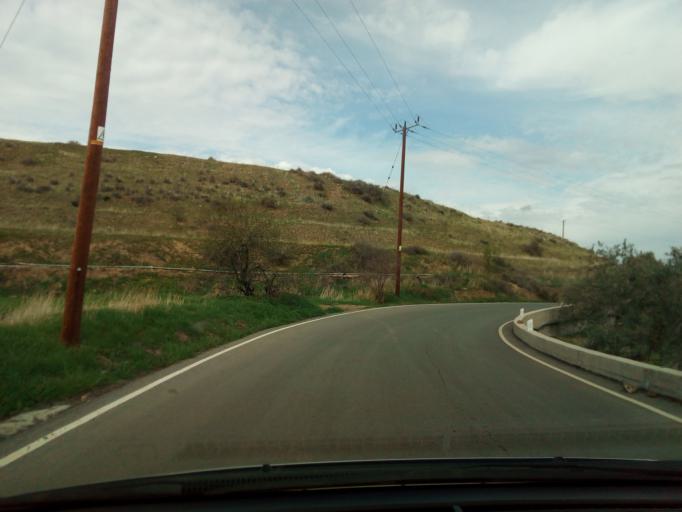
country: CY
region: Lefkosia
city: Astromeritis
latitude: 35.0851
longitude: 32.9941
